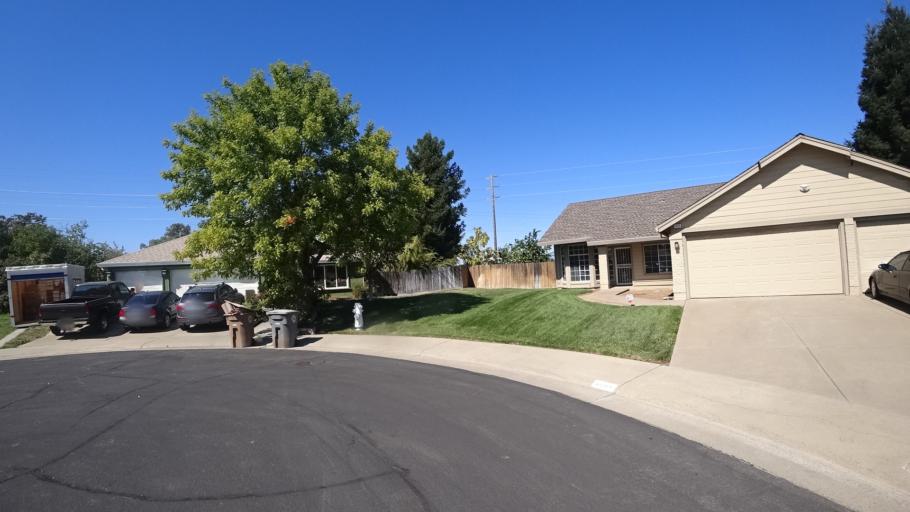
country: US
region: California
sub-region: Sacramento County
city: Laguna
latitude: 38.4375
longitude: -121.4331
